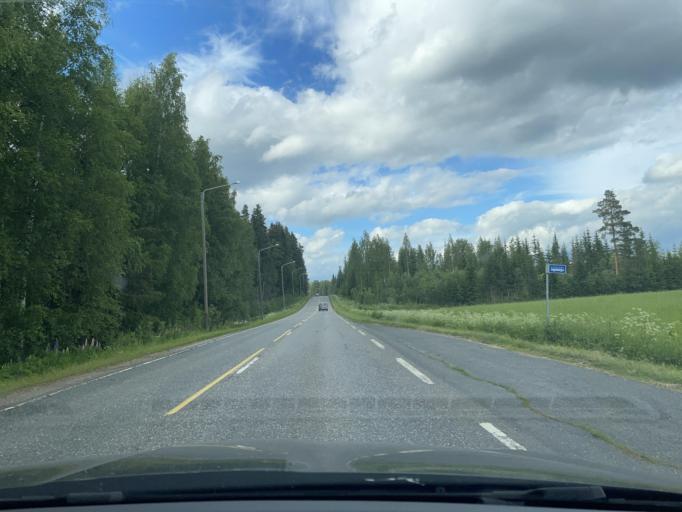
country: FI
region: Central Finland
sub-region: Jaemsae
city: Jaemsaenkoski
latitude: 61.9640
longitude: 25.1580
